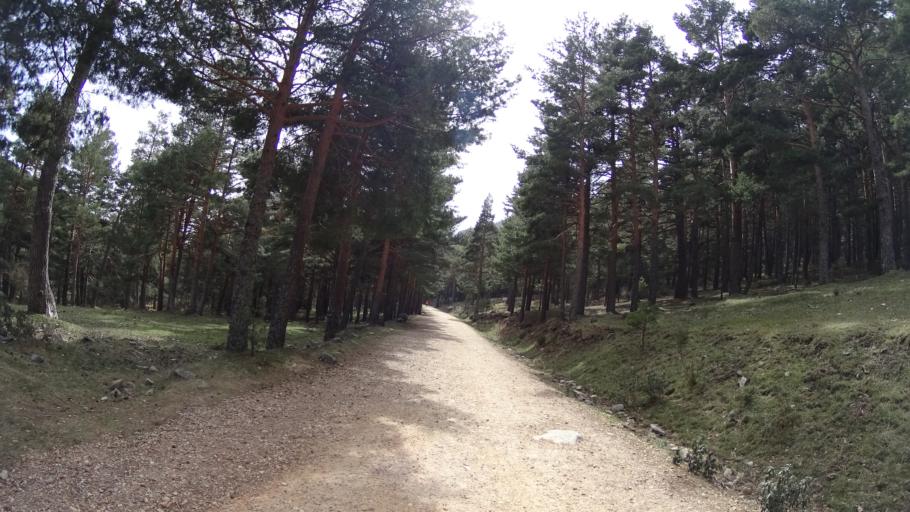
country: ES
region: Madrid
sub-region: Provincia de Madrid
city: Navacerrada
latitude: 40.7658
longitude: -3.9955
